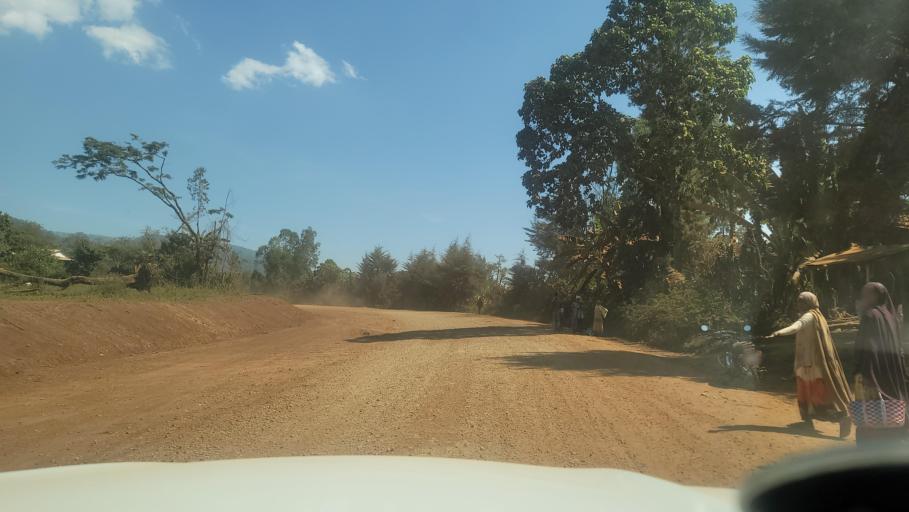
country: ET
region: Oromiya
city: Agaro
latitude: 7.7796
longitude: 36.3453
